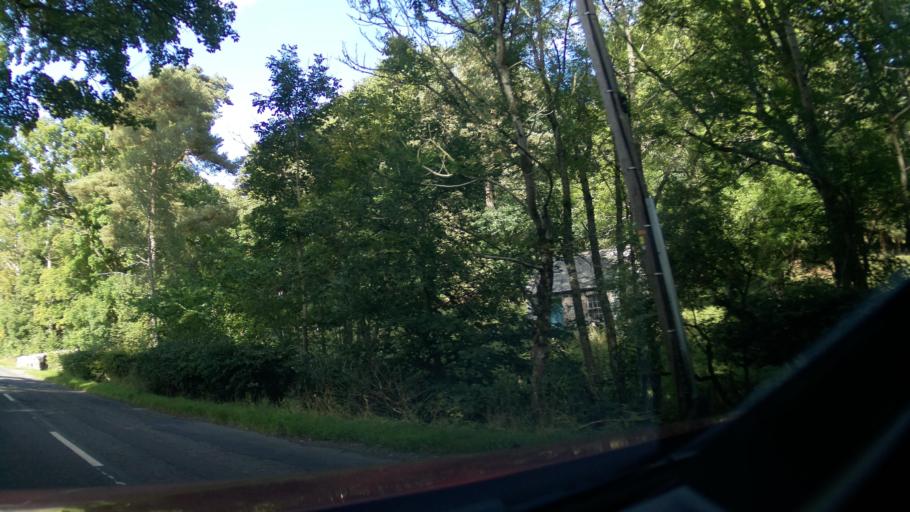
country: GB
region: Scotland
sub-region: South Lanarkshire
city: Biggar
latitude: 55.6171
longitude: -3.4120
